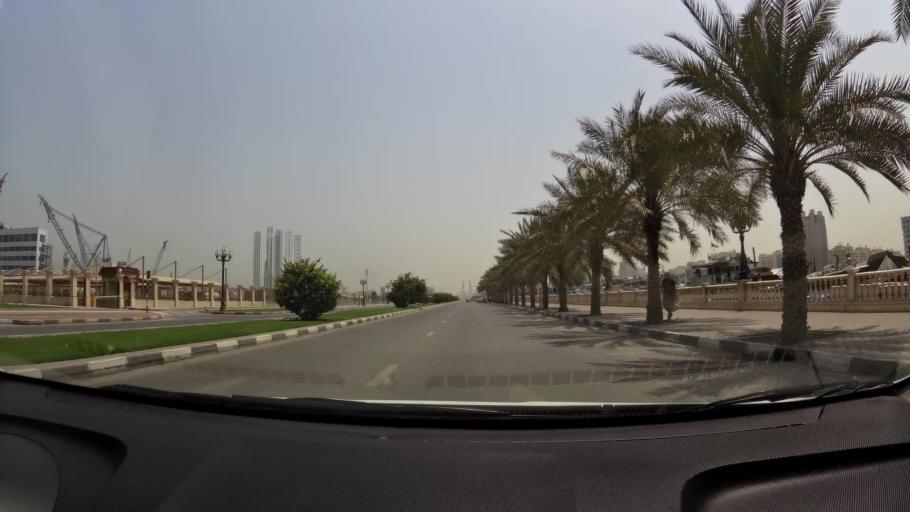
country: AE
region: Ash Shariqah
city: Sharjah
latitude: 25.3596
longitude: 55.3787
